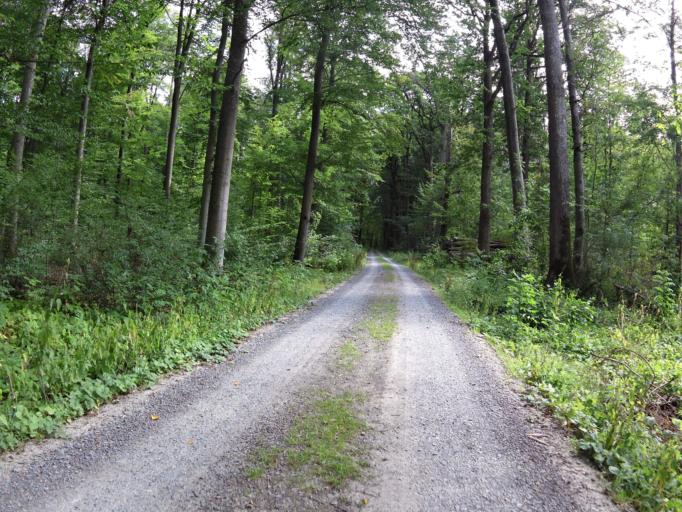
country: DE
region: Bavaria
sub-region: Regierungsbezirk Unterfranken
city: Waldbrunn
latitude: 49.7179
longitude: 9.8014
